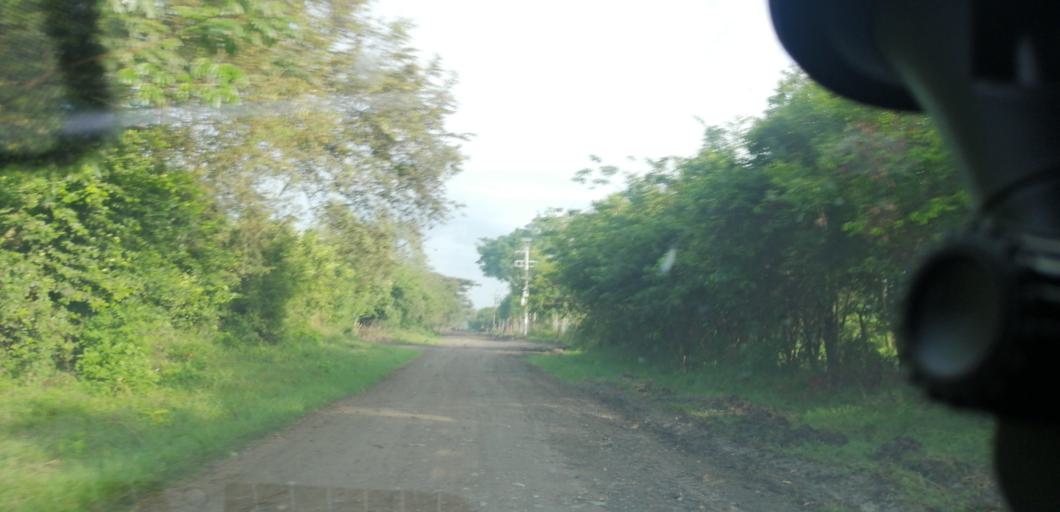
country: CO
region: Valle del Cauca
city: Palmira
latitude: 3.5420
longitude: -76.3602
